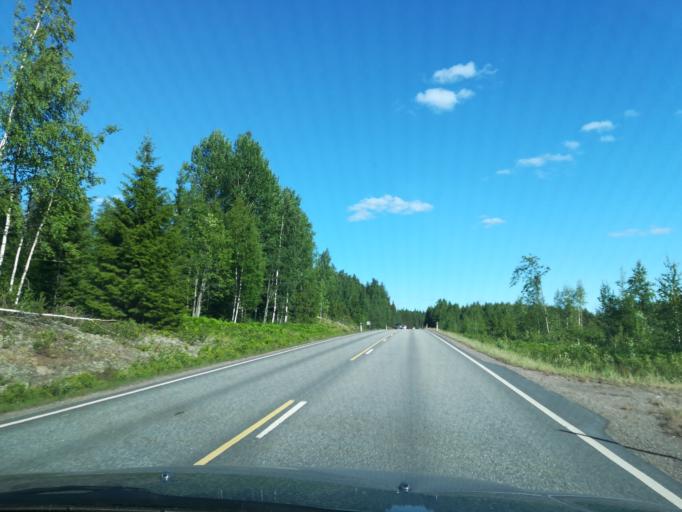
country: FI
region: South Karelia
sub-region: Imatra
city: Ruokolahti
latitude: 61.3915
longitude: 28.6401
